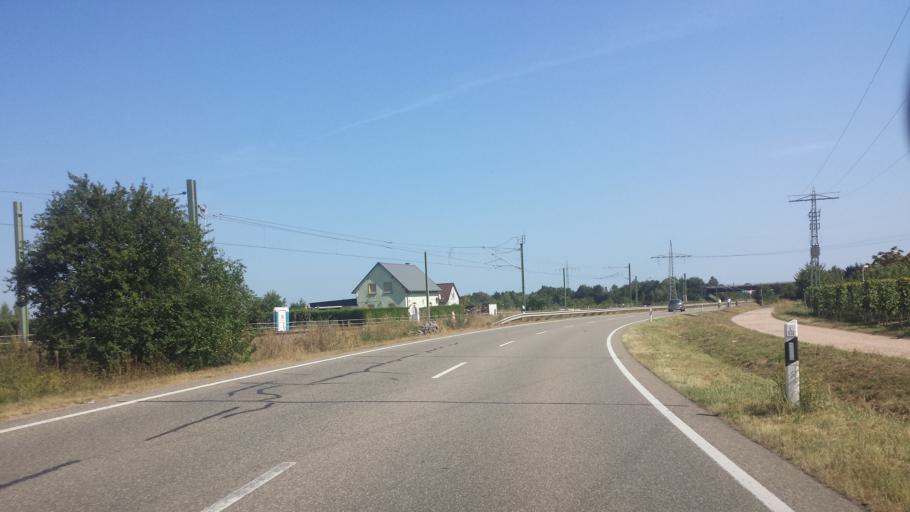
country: DE
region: Rheinland-Pfalz
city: Lachen-Speyerdorf
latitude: 49.3624
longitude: 8.1924
